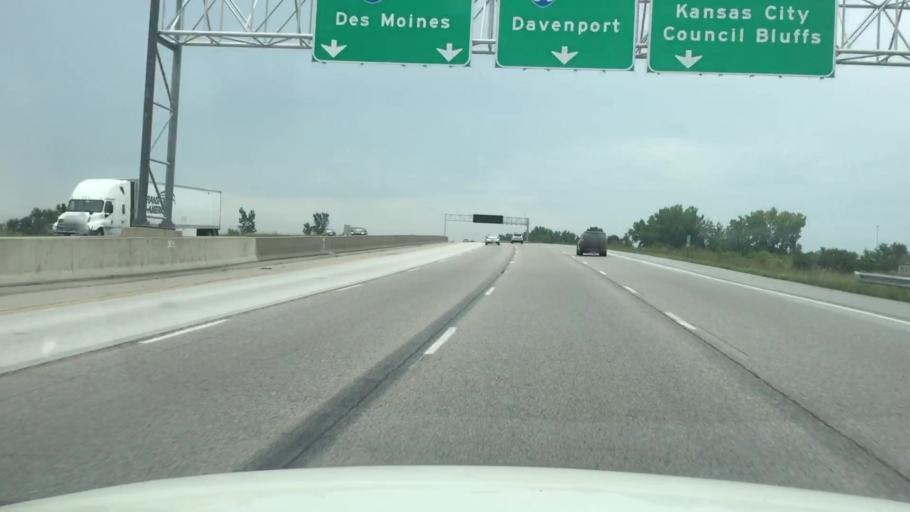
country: US
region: Iowa
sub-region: Polk County
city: Saylorville
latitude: 41.6726
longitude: -93.5781
